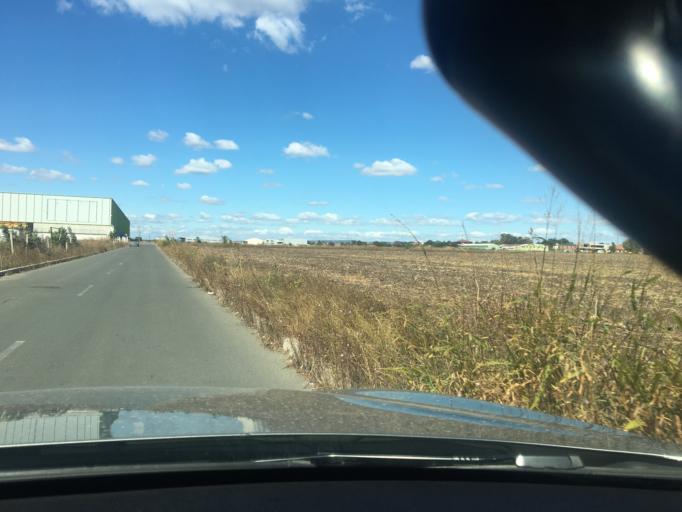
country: BG
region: Burgas
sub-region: Obshtina Burgas
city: Burgas
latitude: 42.5327
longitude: 27.4544
